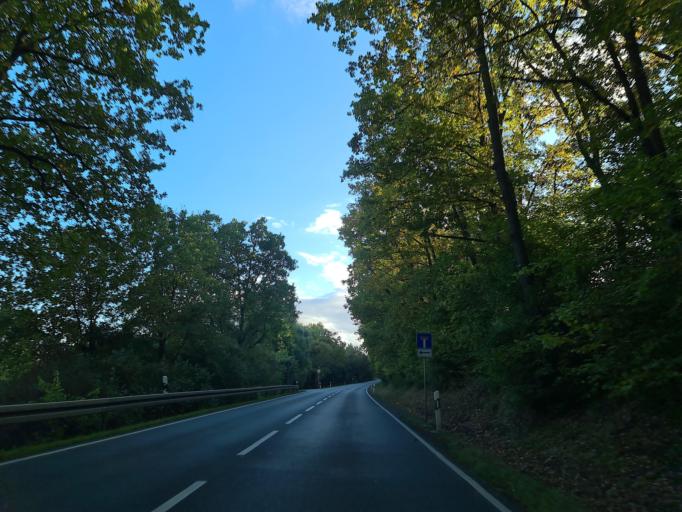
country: DE
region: Thuringia
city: Wunschendorf
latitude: 50.8204
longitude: 12.0775
